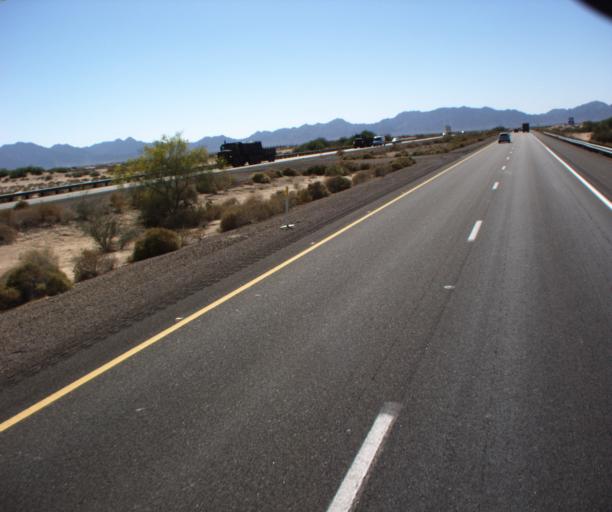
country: US
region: Arizona
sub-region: Yuma County
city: Wellton
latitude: 32.6604
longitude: -114.1494
